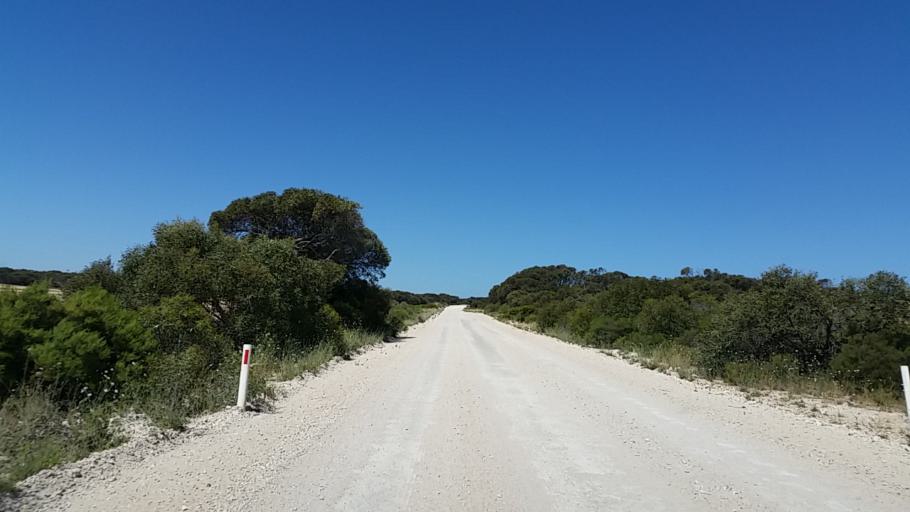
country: AU
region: South Australia
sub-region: Yorke Peninsula
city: Honiton
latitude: -35.2204
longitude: 137.0788
